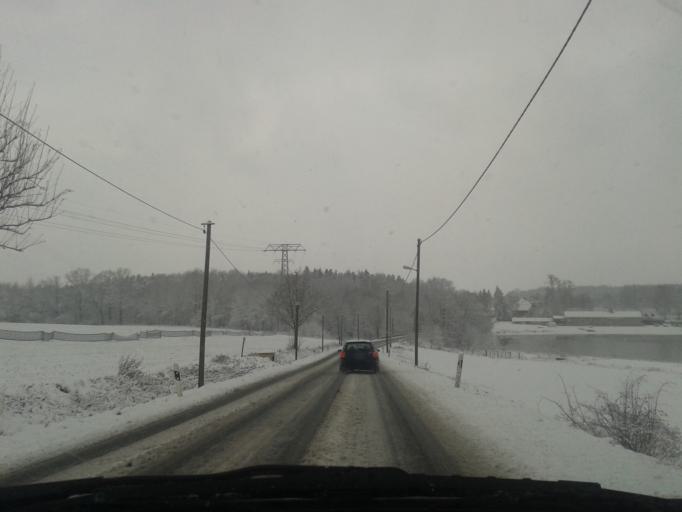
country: DE
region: Saxony
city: Radeberg
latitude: 51.0596
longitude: 13.9355
